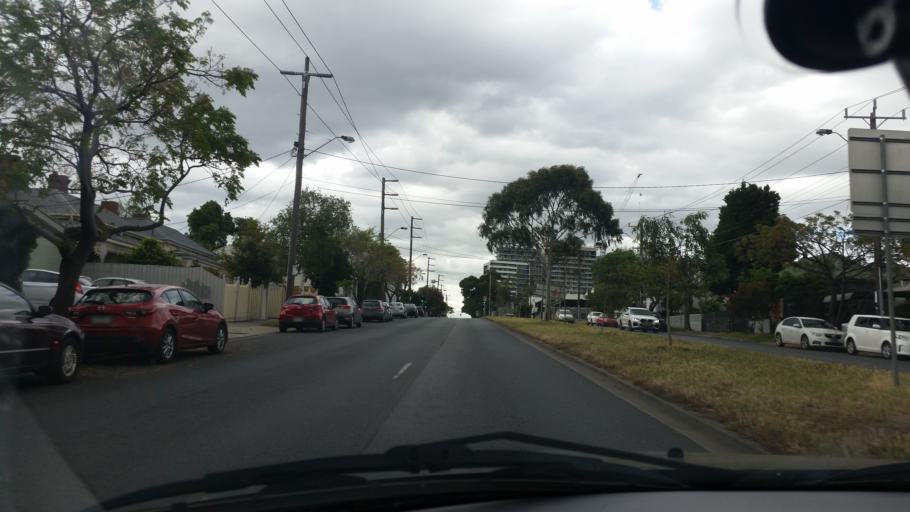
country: AU
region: Victoria
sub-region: Maribyrnong
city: Footscray
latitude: -37.8041
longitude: 144.9047
